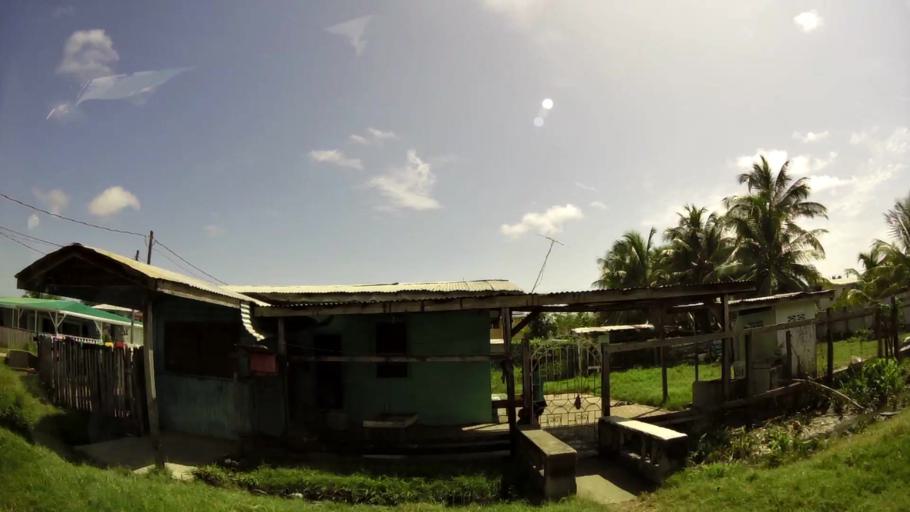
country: GY
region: Demerara-Mahaica
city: Mahaica Village
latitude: 6.7690
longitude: -58.0069
